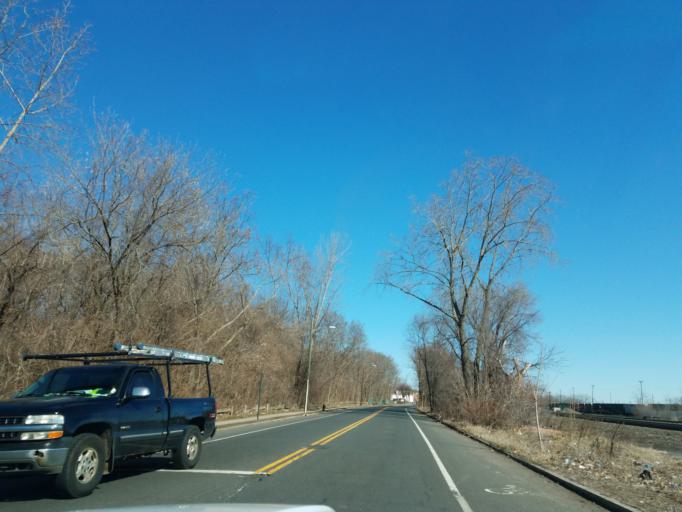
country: US
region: Connecticut
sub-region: Hartford County
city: Hartford
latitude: 41.7784
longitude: -72.6725
